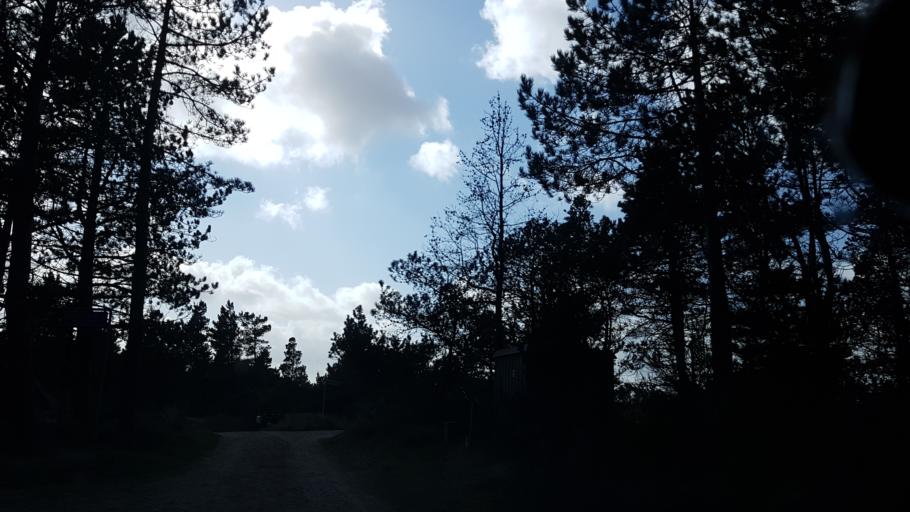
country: DE
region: Schleswig-Holstein
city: List
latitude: 55.1003
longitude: 8.5389
